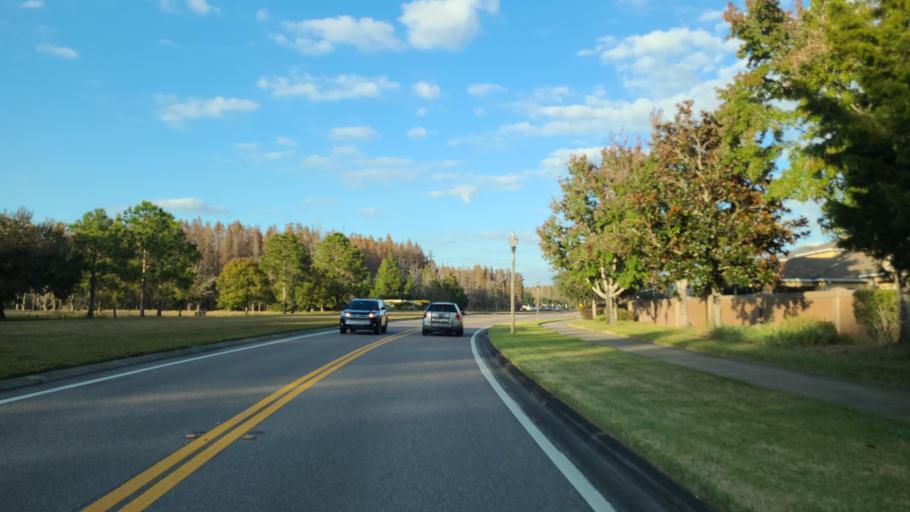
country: US
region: Florida
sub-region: Hillsborough County
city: Cheval
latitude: 28.2018
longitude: -82.5242
